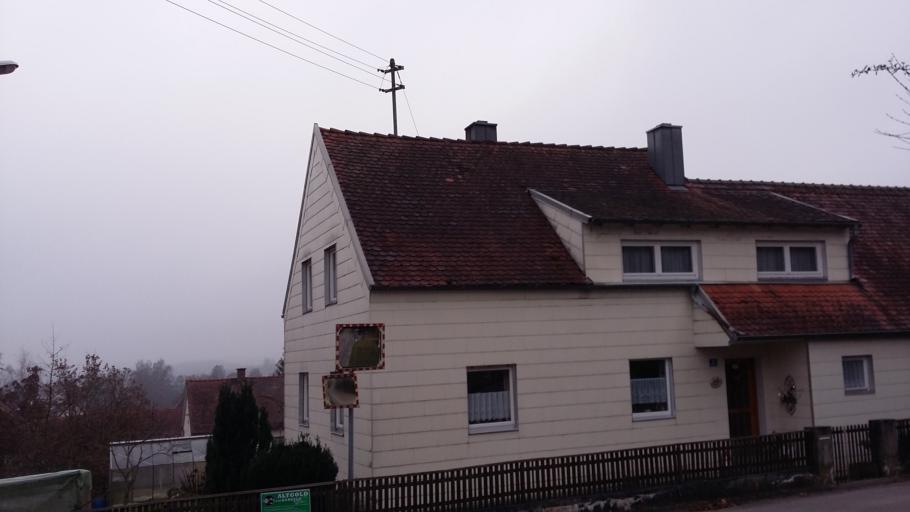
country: DE
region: Bavaria
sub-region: Swabia
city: Pottmes
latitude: 48.5825
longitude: 11.0833
